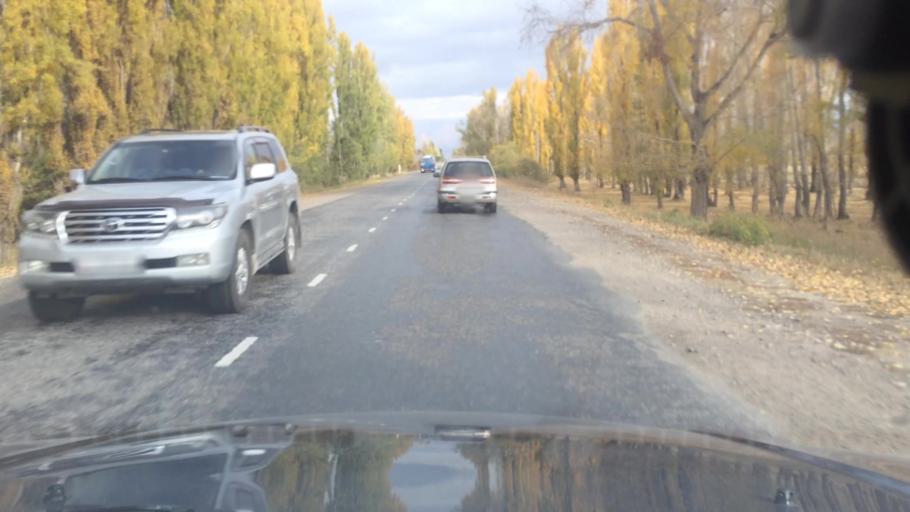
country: KG
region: Ysyk-Koel
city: Tyup
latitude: 42.6143
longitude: 78.3659
